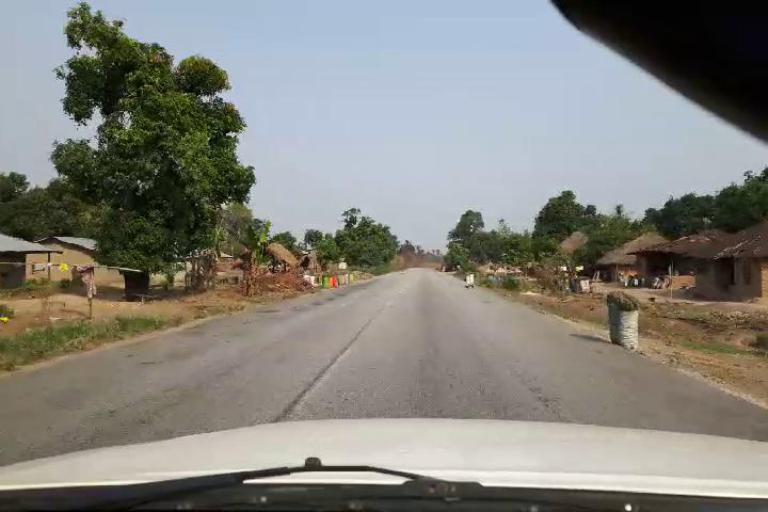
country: SL
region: Southern Province
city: Baiima
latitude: 8.1420
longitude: -11.9001
